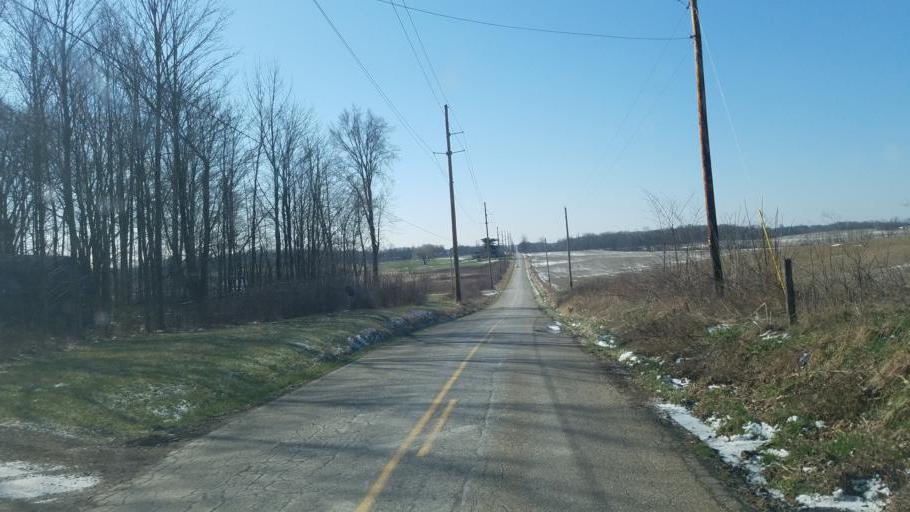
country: US
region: Ohio
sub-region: Knox County
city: Mount Vernon
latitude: 40.3195
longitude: -82.4723
